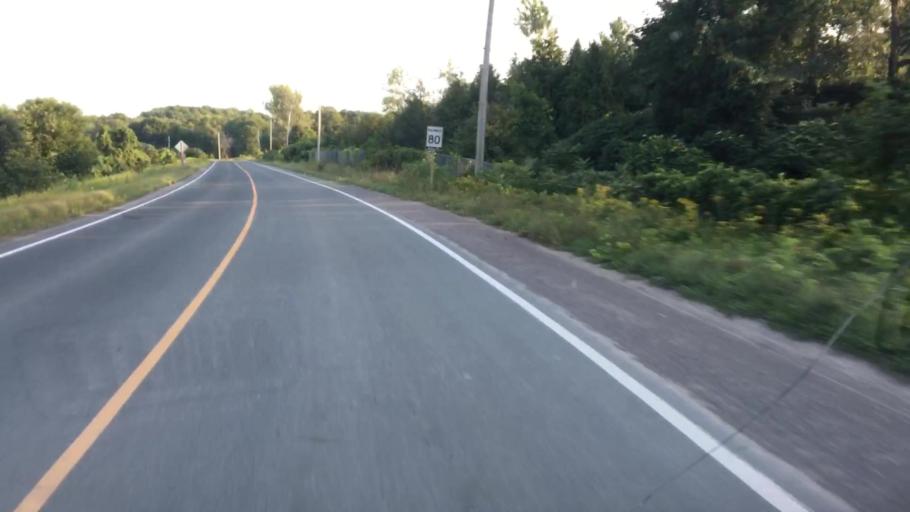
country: CA
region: Ontario
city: Quinte West
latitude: 44.0990
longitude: -77.7358
